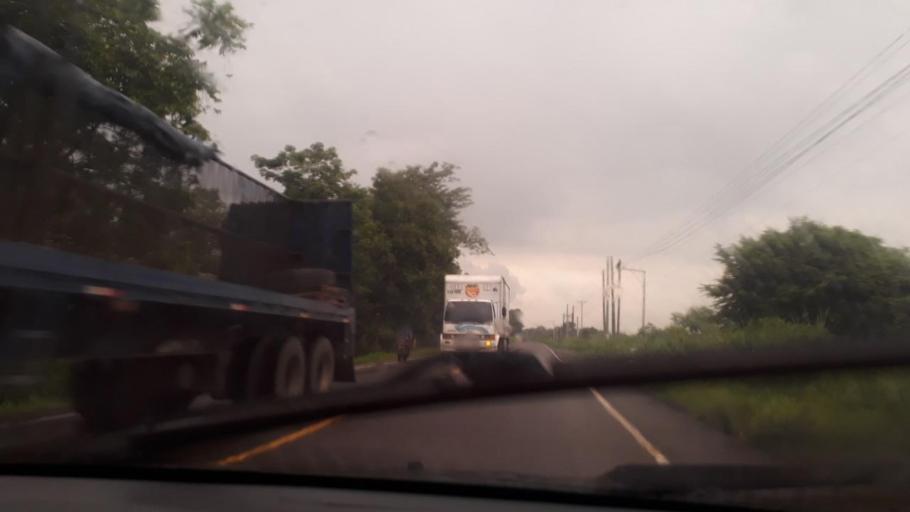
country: GT
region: Escuintla
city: Guanagazapa
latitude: 14.0993
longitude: -90.6087
